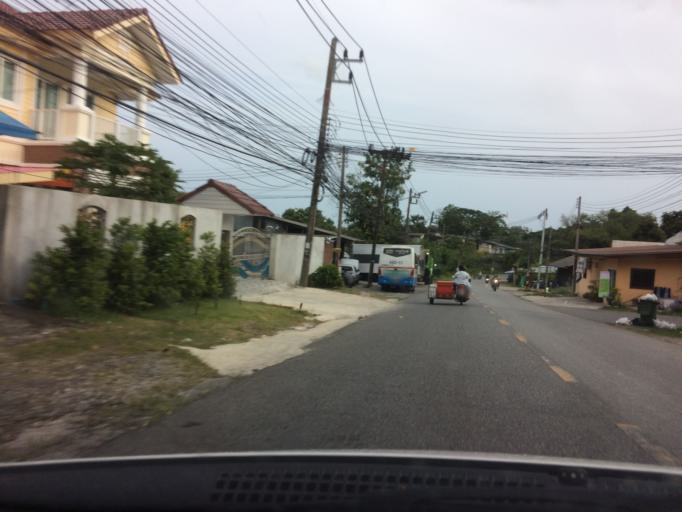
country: TH
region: Phuket
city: Phuket
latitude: 7.8922
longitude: 98.4071
